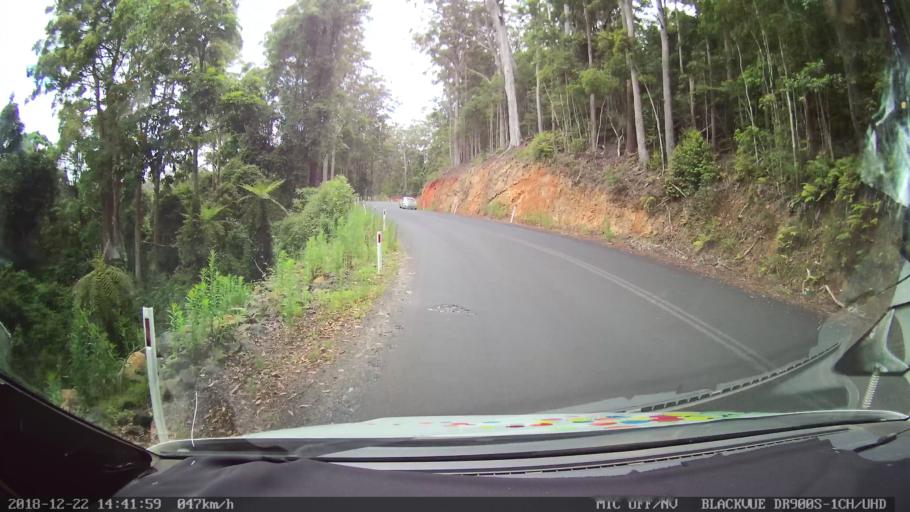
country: AU
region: New South Wales
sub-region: Bellingen
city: Dorrigo
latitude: -30.1563
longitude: 152.5863
